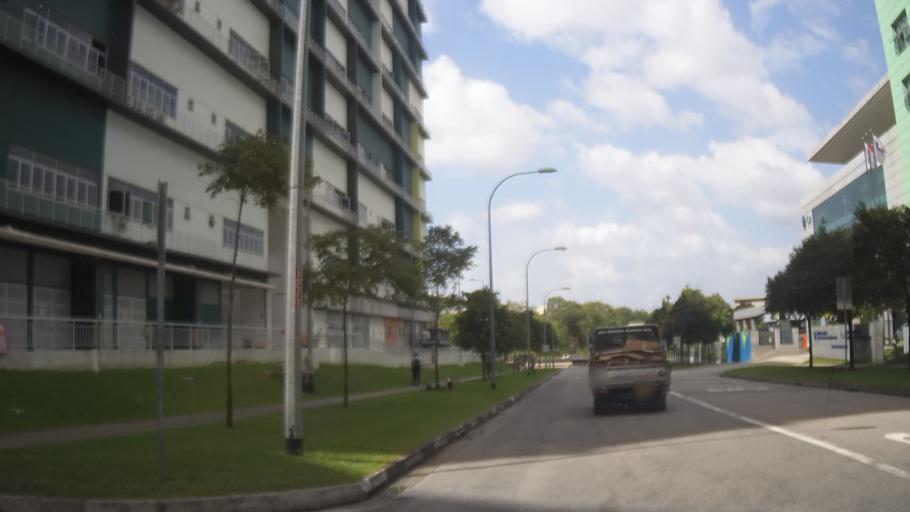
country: MY
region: Johor
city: Johor Bahru
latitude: 1.4090
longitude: 103.7571
